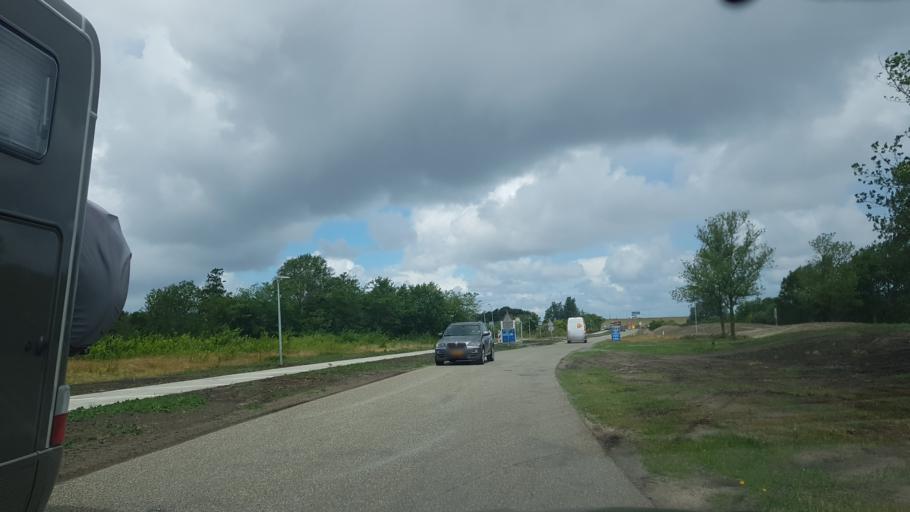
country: NL
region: Friesland
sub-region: Gemeente Dongeradeel
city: Anjum
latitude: 53.4043
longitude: 6.2127
